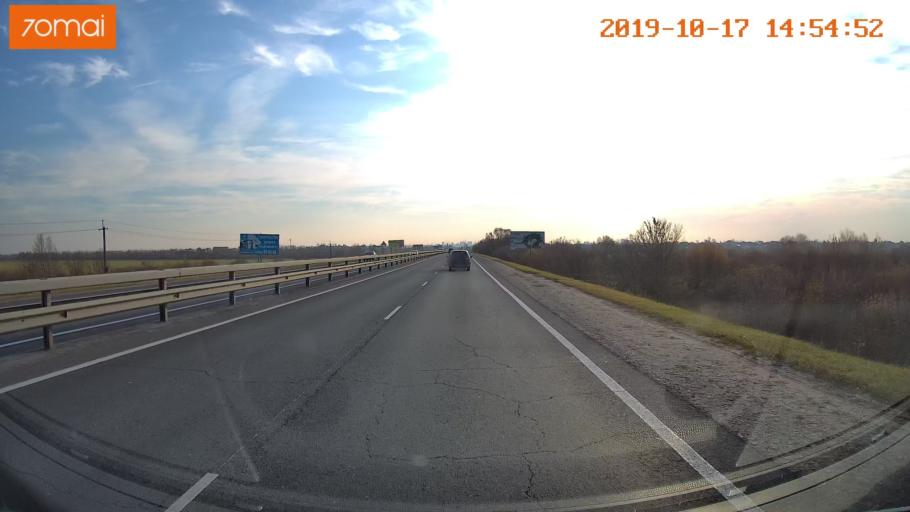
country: RU
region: Rjazan
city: Polyany
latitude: 54.6758
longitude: 39.8290
